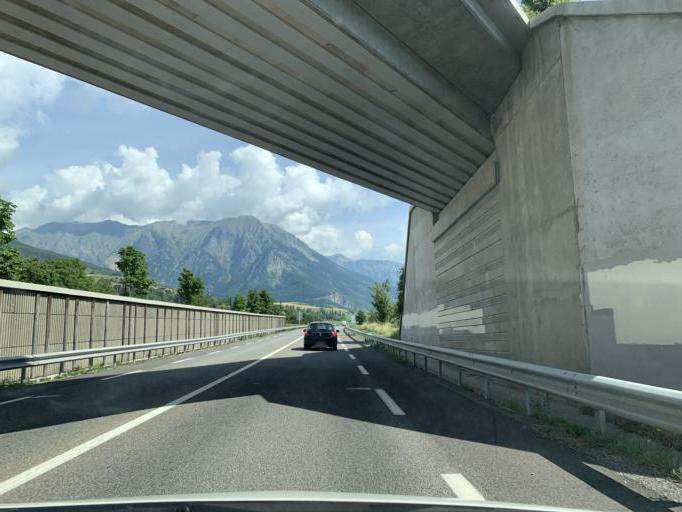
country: FR
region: Provence-Alpes-Cote d'Azur
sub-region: Departement des Hautes-Alpes
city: Embrun
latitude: 44.5833
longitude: 6.5124
